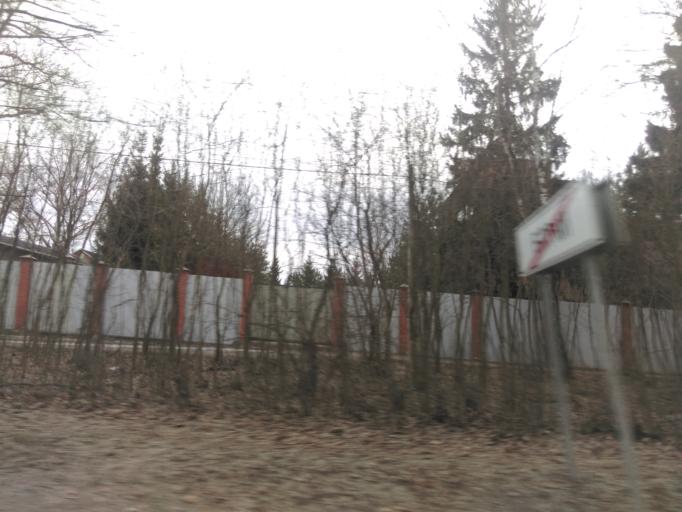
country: RU
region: Moskovskaya
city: Nikolina Gora
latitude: 55.7154
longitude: 37.0959
